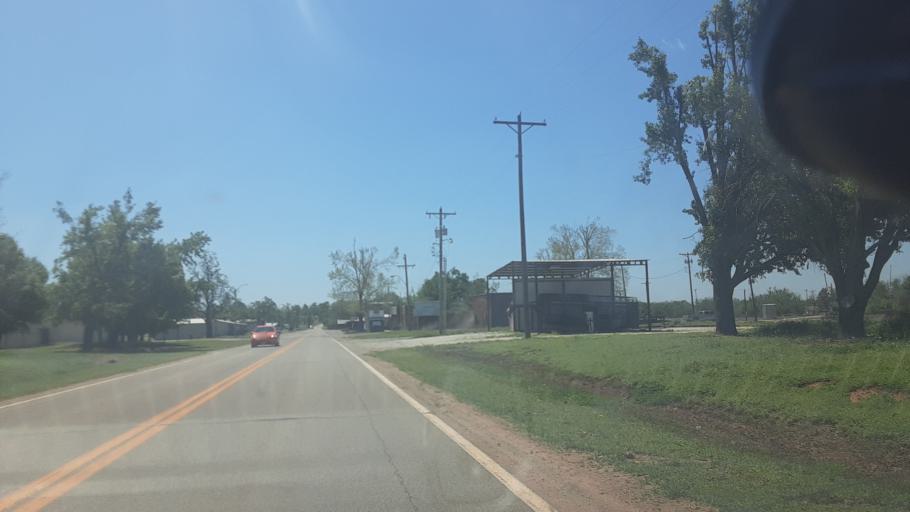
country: US
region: Oklahoma
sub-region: Logan County
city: Guthrie
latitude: 36.0670
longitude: -97.4071
